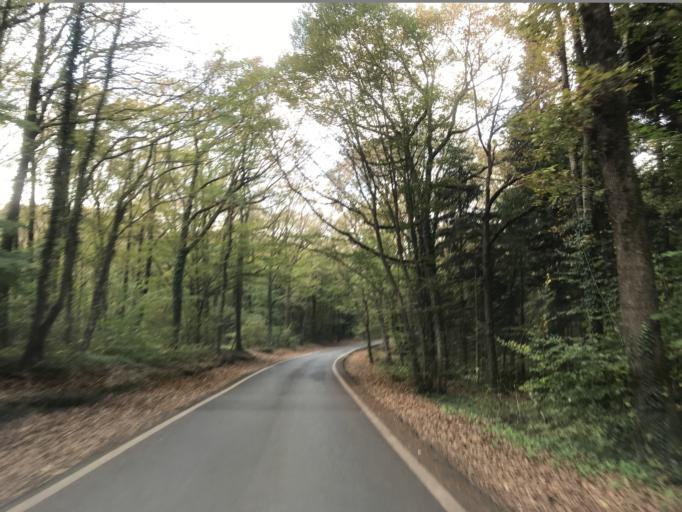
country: TR
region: Istanbul
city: Arikoey
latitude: 41.1883
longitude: 28.9737
